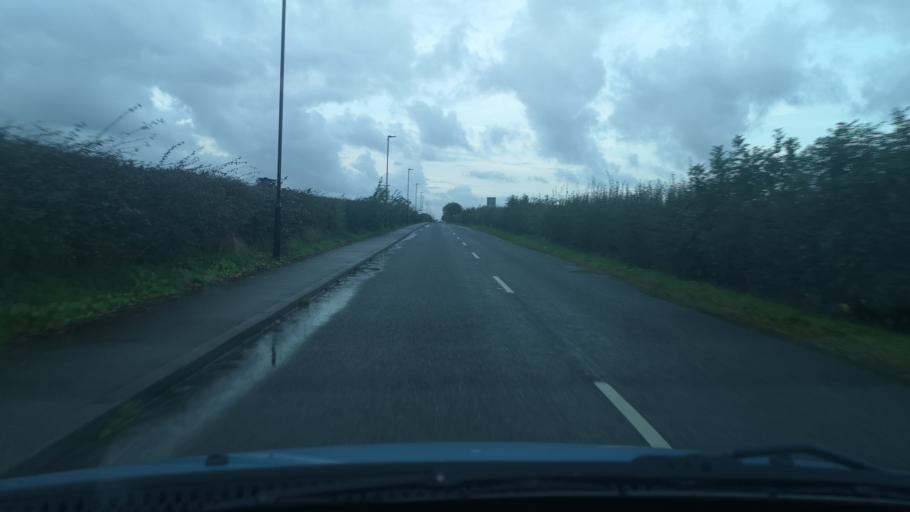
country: GB
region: England
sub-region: Doncaster
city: Norton
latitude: 53.6272
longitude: -1.1824
